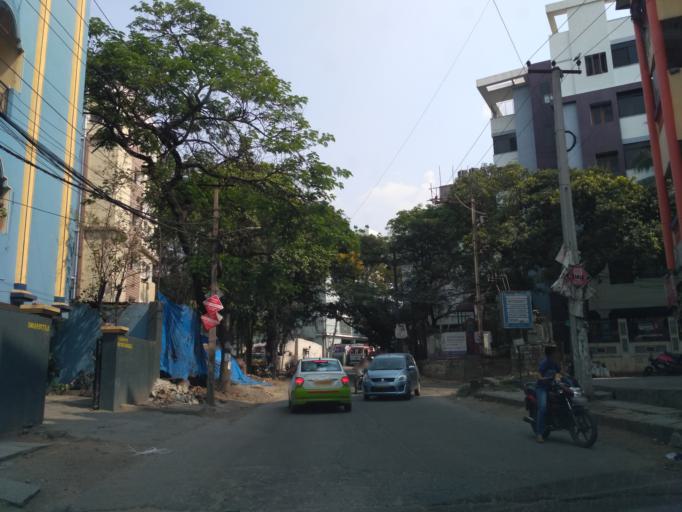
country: IN
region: Telangana
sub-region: Hyderabad
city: Hyderabad
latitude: 17.4312
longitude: 78.4386
